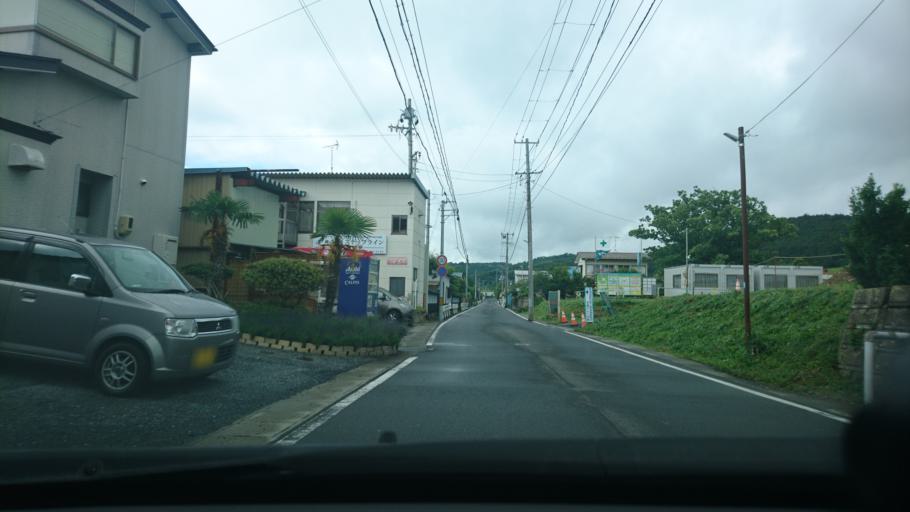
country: JP
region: Miyagi
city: Wakuya
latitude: 38.6567
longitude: 141.2848
